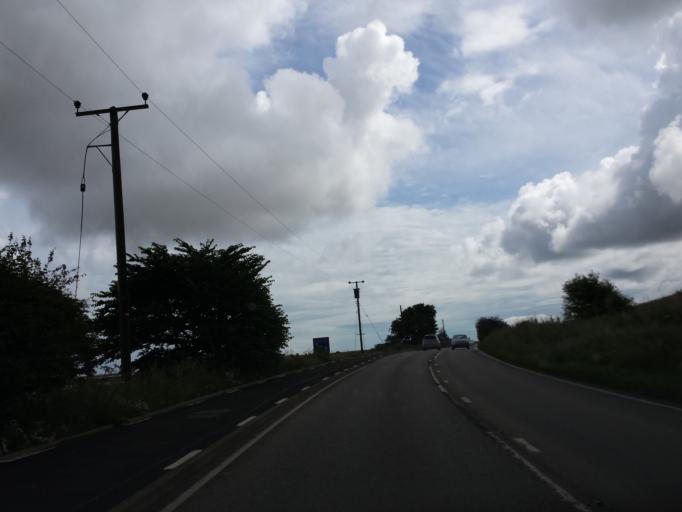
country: GB
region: Scotland
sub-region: Fife
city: Leuchars
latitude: 56.3589
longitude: -2.8737
